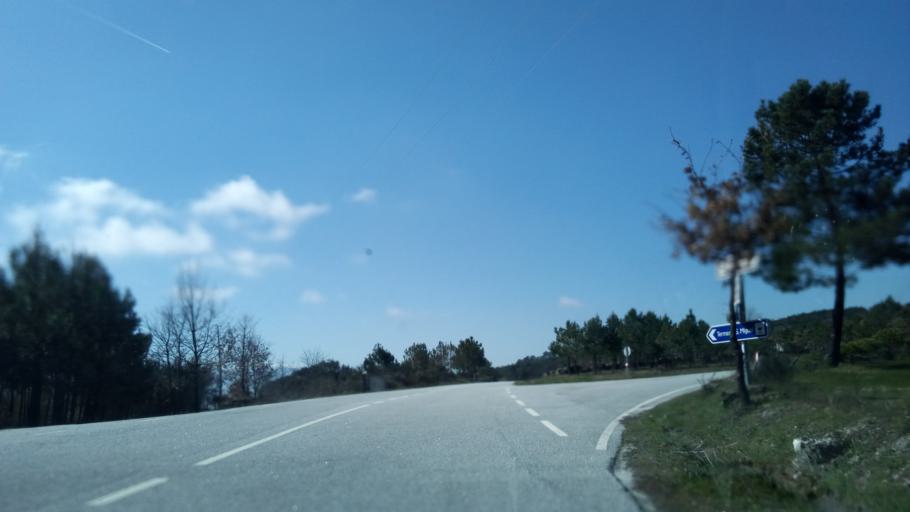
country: PT
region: Guarda
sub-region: Fornos de Algodres
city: Fornos de Algodres
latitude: 40.6396
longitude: -7.5317
